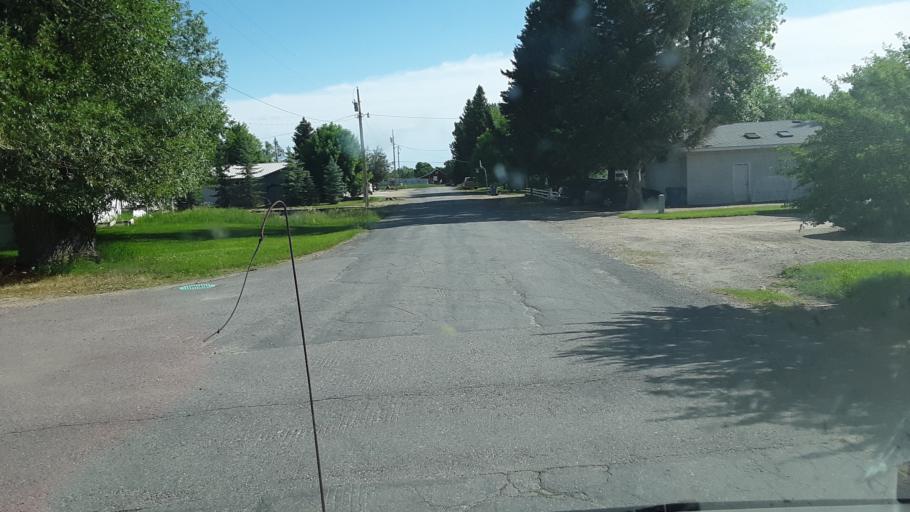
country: US
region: Montana
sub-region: Carbon County
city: Red Lodge
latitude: 45.3586
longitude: -109.1646
